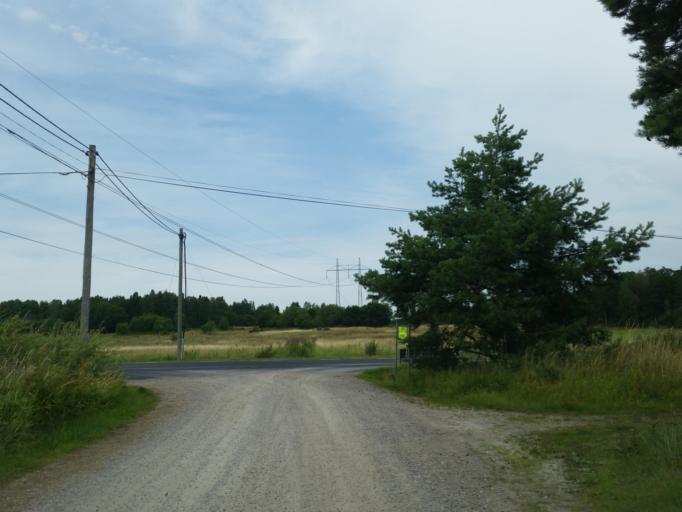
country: SE
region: Soedermanland
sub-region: Strangnas Kommun
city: Akers Styckebruk
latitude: 59.2727
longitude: 17.1363
